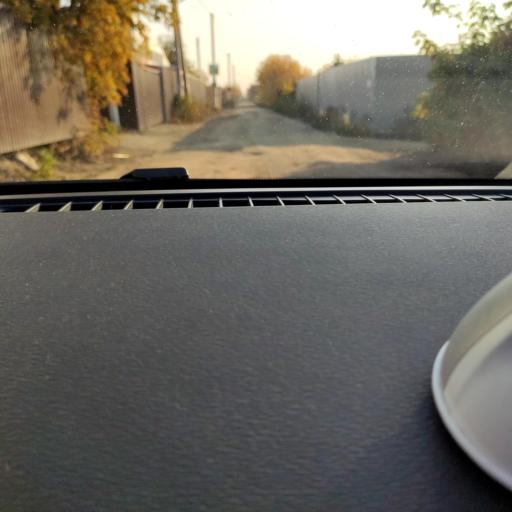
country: RU
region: Samara
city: Petra-Dubrava
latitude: 53.2568
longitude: 50.2670
